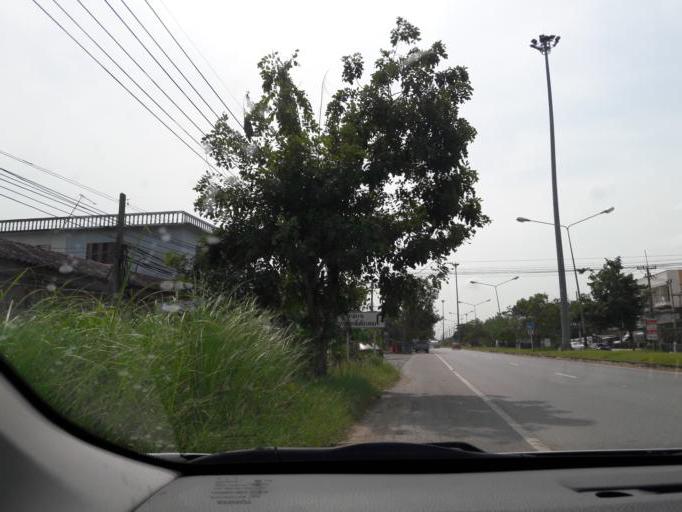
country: TH
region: Ang Thong
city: Ang Thong
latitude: 14.5814
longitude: 100.4530
